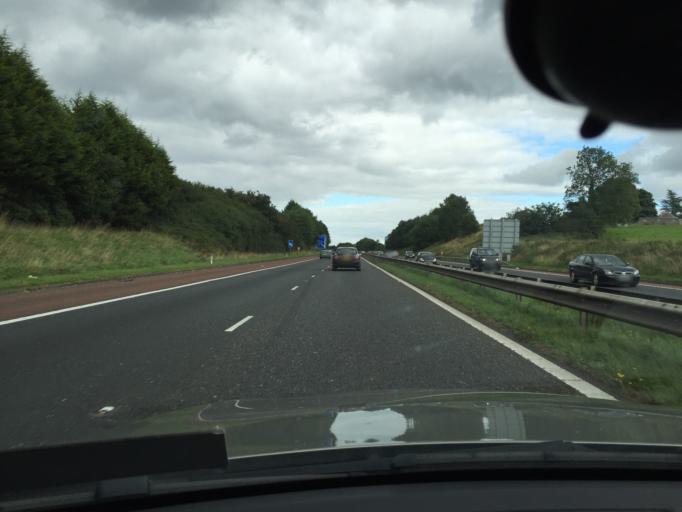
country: GB
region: Northern Ireland
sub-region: Lisburn District
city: Lisburn
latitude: 54.5004
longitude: -6.0369
